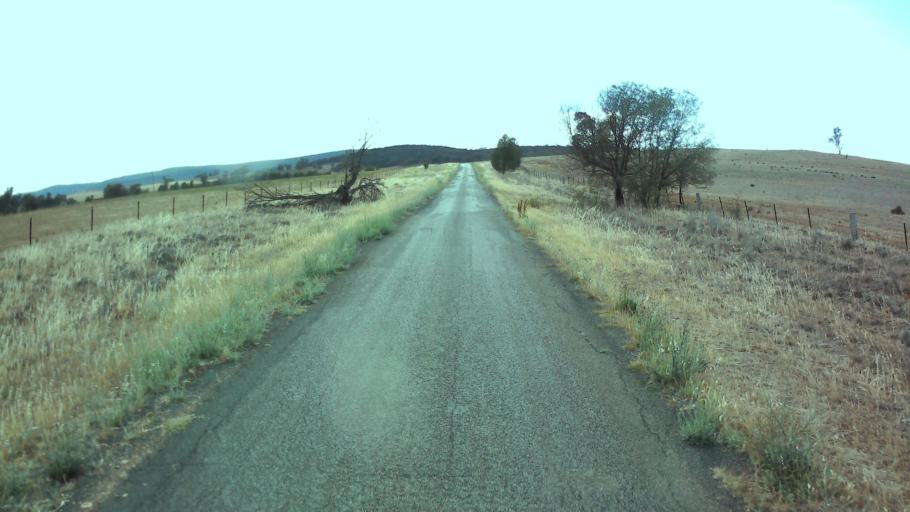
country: AU
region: New South Wales
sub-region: Weddin
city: Grenfell
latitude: -33.8436
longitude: 148.2554
